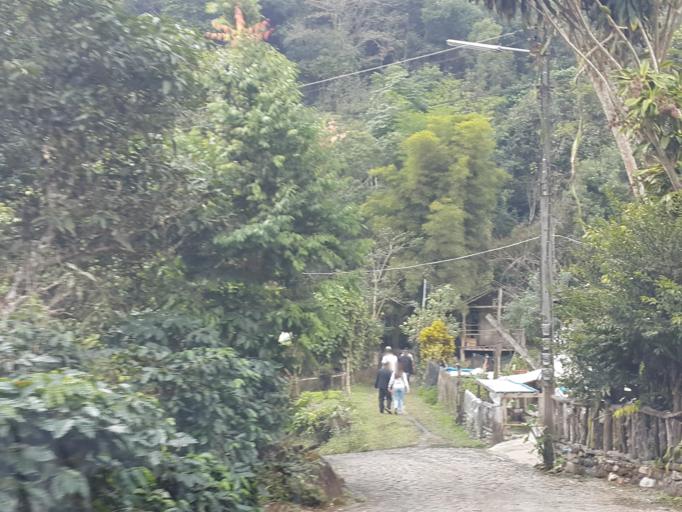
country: TH
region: Chiang Mai
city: Mae On
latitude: 18.9008
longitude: 99.3567
